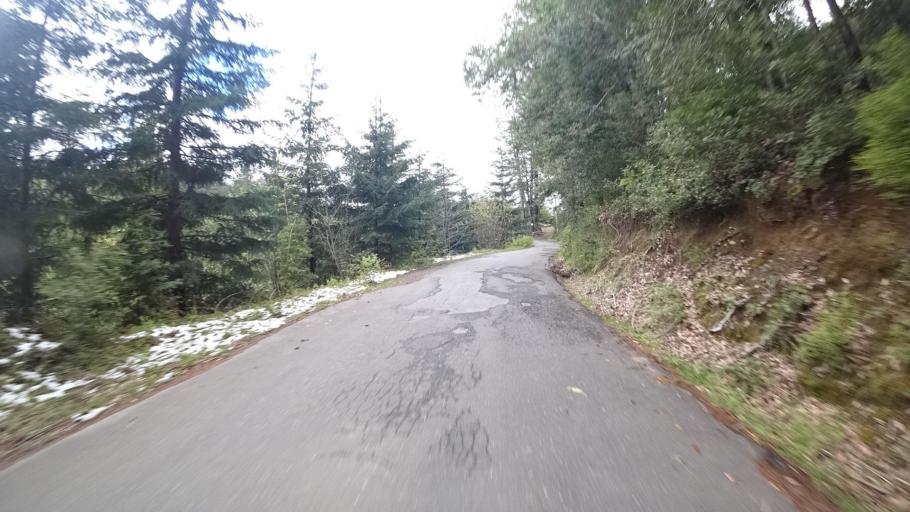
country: US
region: California
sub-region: Humboldt County
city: Blue Lake
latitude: 40.8731
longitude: -123.8883
